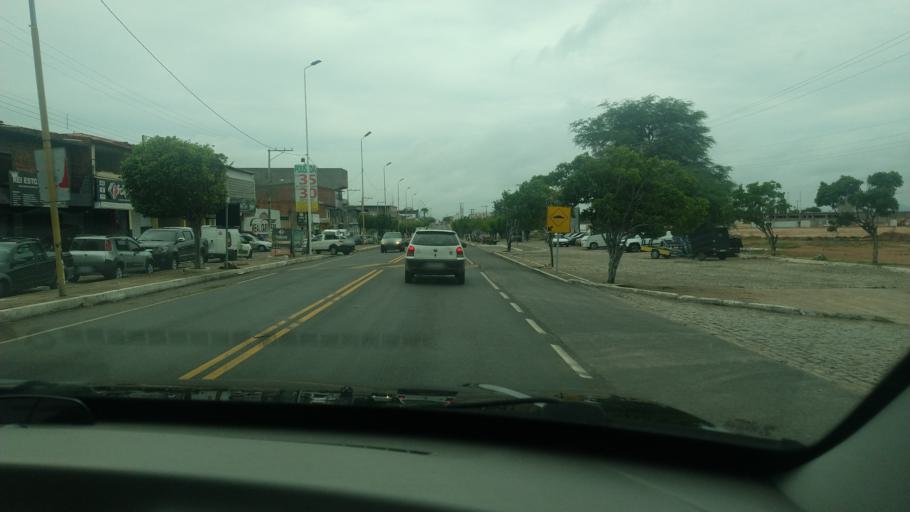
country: BR
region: Bahia
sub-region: Paulo Afonso
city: Paulo Afonso
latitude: -9.4051
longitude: -38.2379
